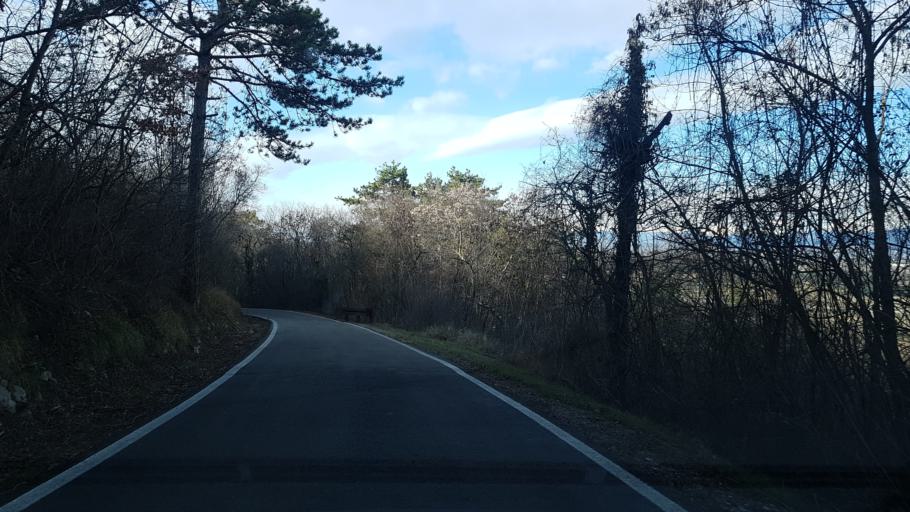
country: IT
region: Friuli Venezia Giulia
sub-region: Provincia di Gorizia
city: Savogna d'Isonzo
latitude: 45.8942
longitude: 13.5487
